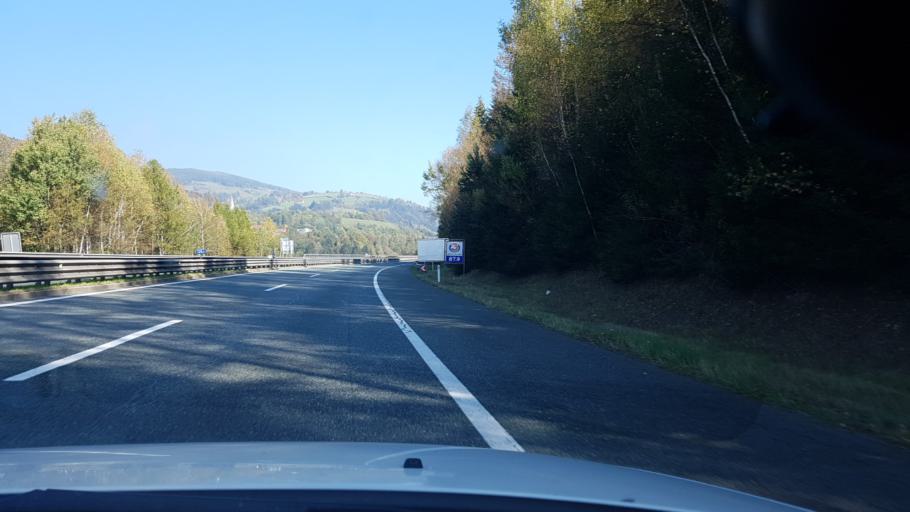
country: AT
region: Carinthia
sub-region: Politischer Bezirk Spittal an der Drau
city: Gmuend
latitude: 46.9064
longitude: 13.5446
